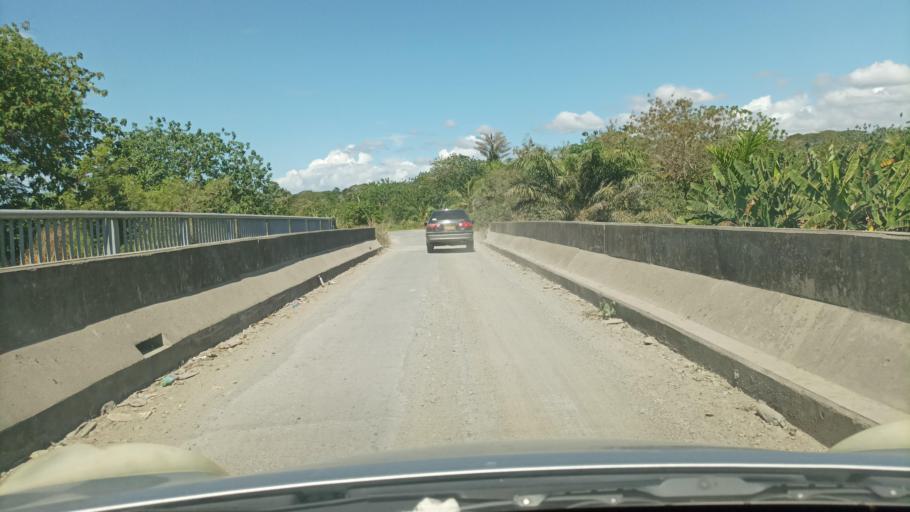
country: SB
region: Guadalcanal
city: Honiara
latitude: -9.4401
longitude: 160.0833
